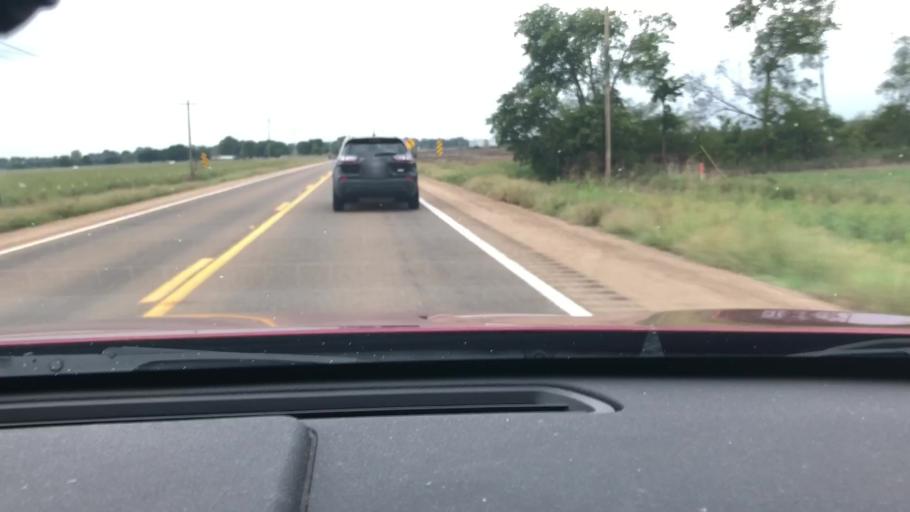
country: US
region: Arkansas
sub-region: Lafayette County
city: Lewisville
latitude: 33.3813
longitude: -93.7366
